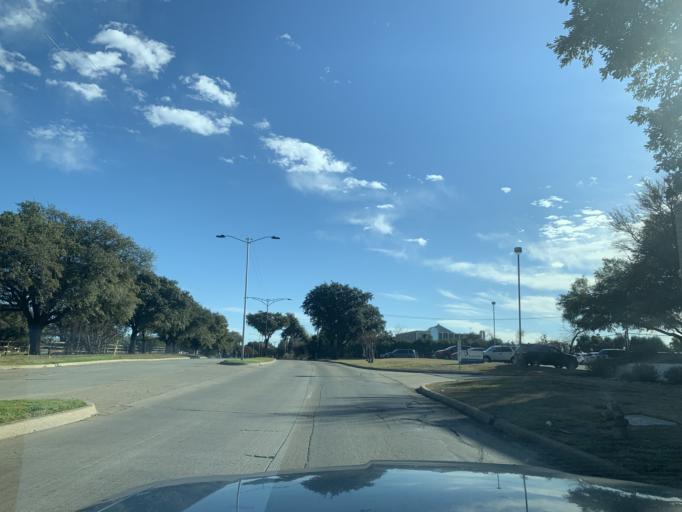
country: US
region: Texas
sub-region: Tarrant County
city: Arlington
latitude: 32.7618
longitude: -97.0603
